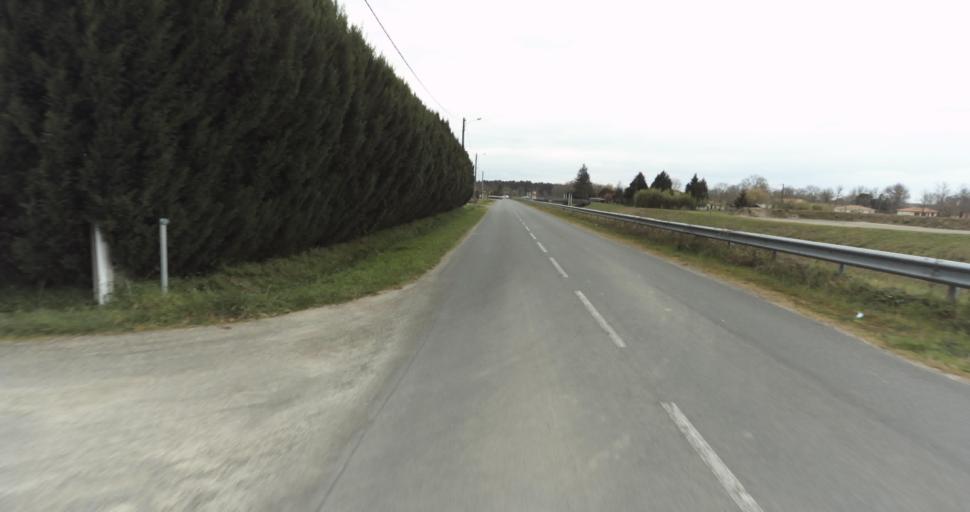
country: FR
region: Aquitaine
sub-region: Departement des Landes
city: Roquefort
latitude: 44.0245
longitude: -0.3319
